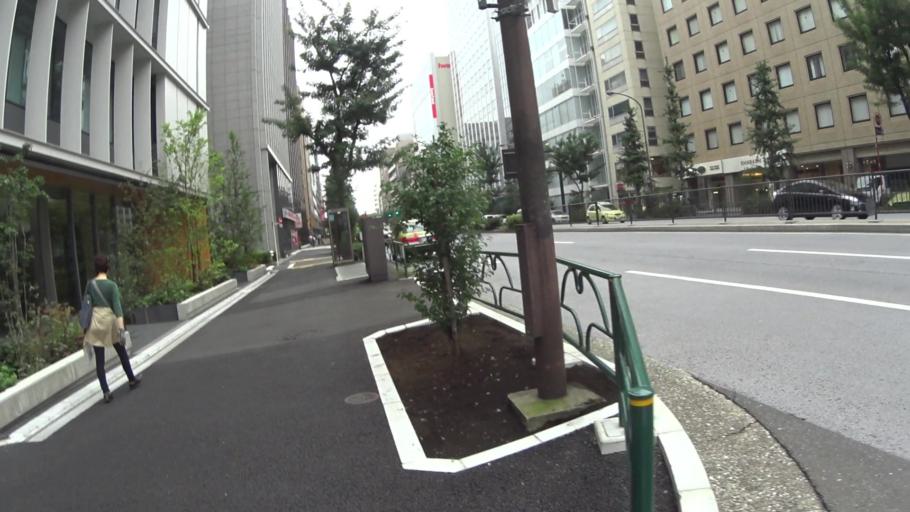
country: JP
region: Tokyo
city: Tokyo
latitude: 35.6643
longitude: 139.7530
